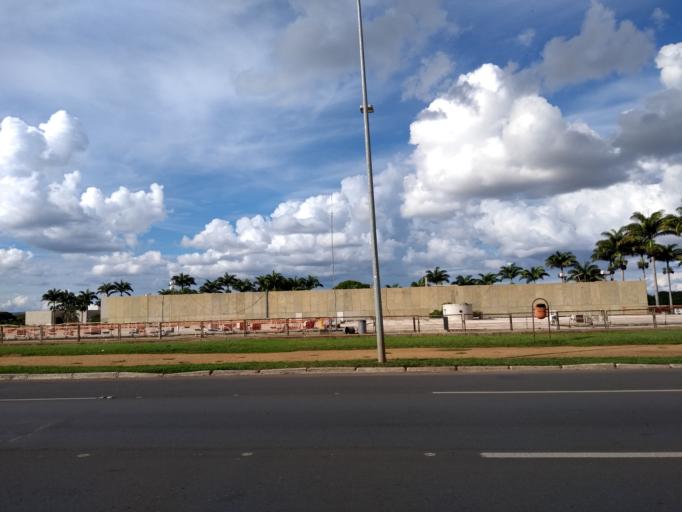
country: BR
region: Federal District
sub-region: Brasilia
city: Brasilia
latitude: -15.7984
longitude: -47.8644
